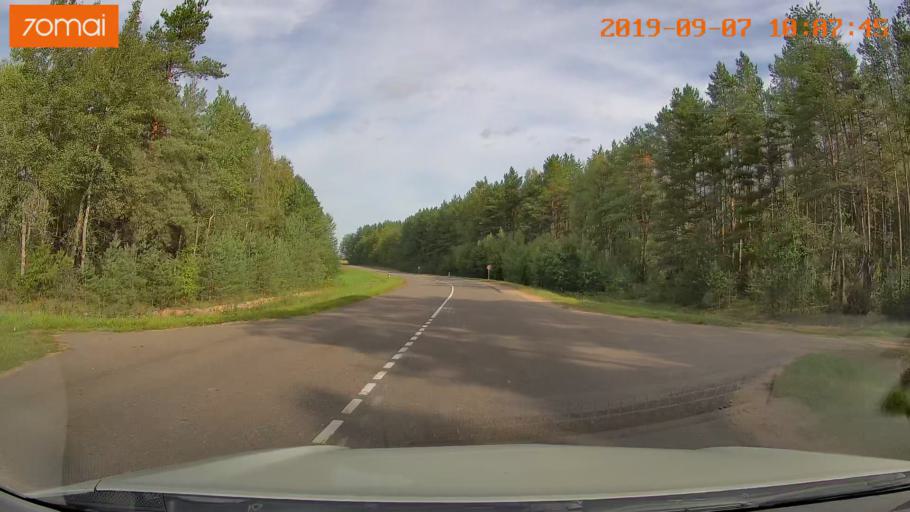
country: BY
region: Grodnenskaya
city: Voranava
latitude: 54.0796
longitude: 25.3955
